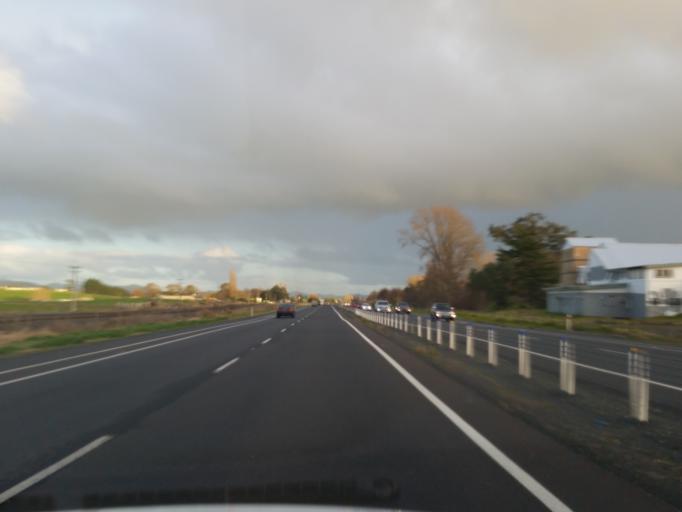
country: NZ
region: Waikato
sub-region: Waikato District
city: Te Kauwhata
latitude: -37.4641
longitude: 175.1569
